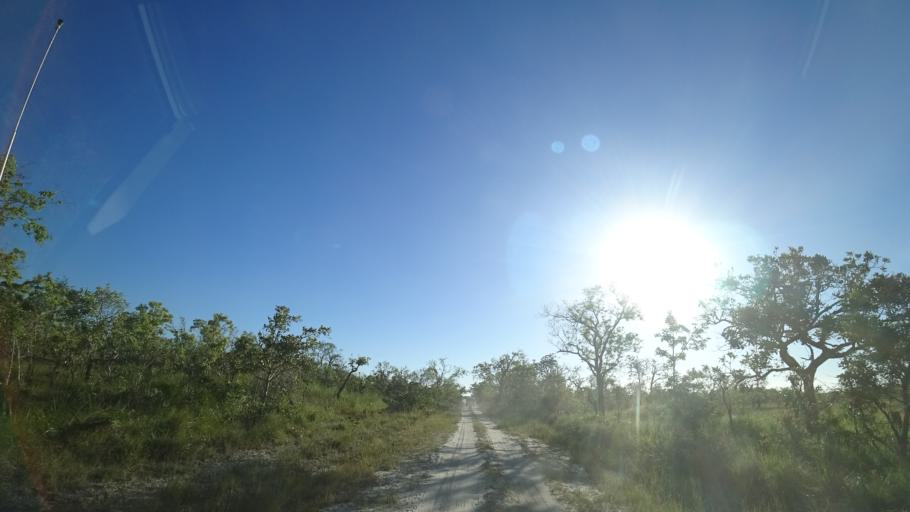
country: MZ
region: Sofala
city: Beira
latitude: -19.5755
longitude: 35.2115
